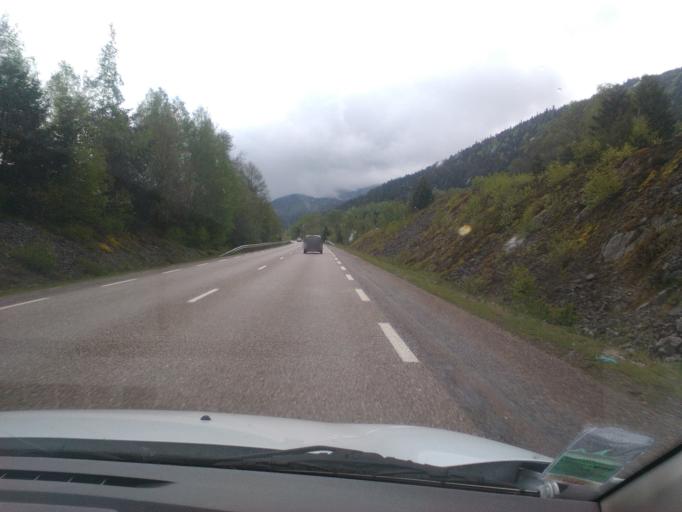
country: FR
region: Lorraine
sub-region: Departement des Vosges
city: Saulxures-sur-Moselotte
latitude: 47.9459
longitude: 6.7952
